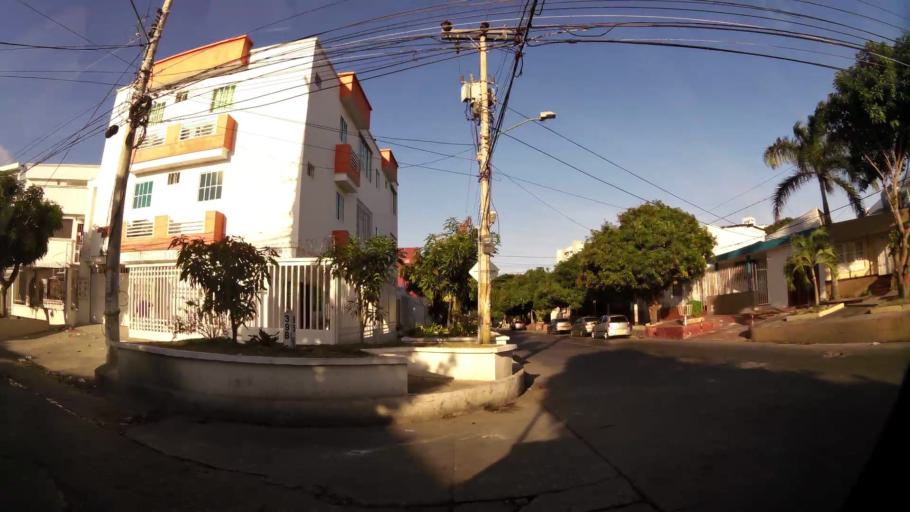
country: CO
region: Atlantico
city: Barranquilla
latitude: 10.9849
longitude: -74.8008
